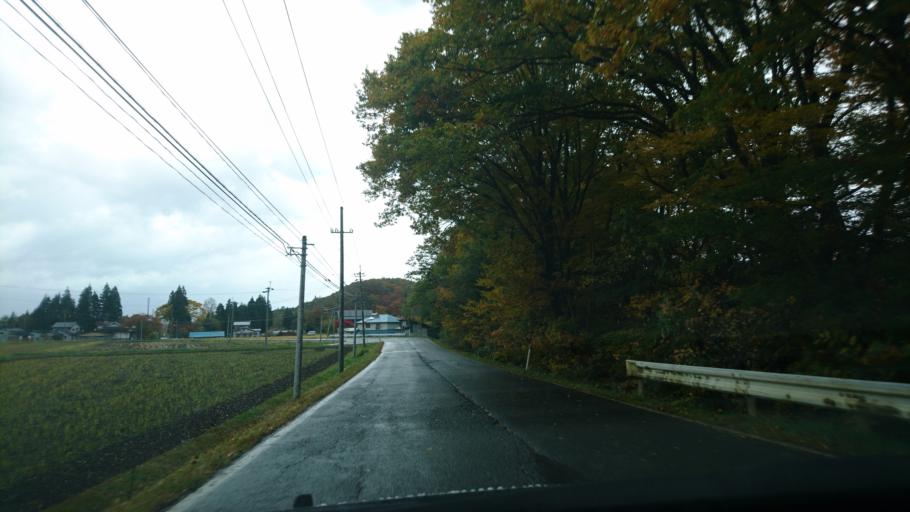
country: JP
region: Iwate
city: Shizukuishi
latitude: 39.6210
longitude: 140.9471
